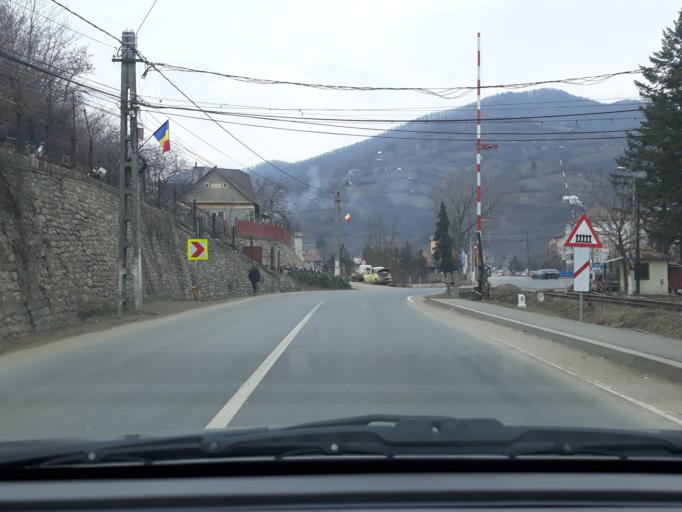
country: RO
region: Salaj
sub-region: Oras Simleu Silvaniei
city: Simleu Silvaniei
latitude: 47.2313
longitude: 22.7834
